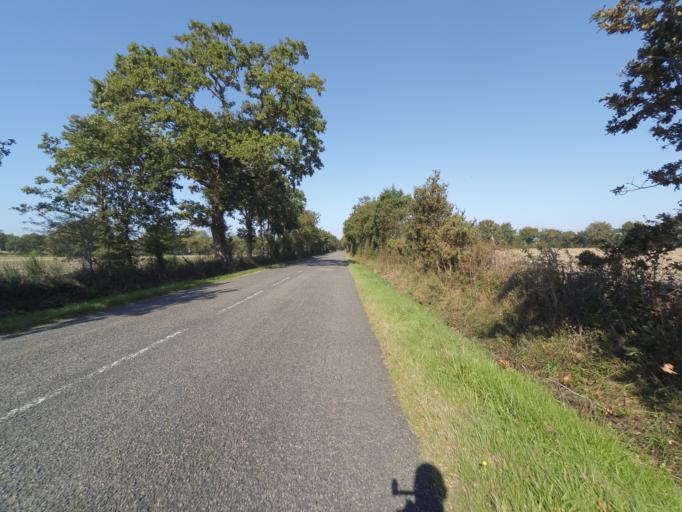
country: FR
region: Pays de la Loire
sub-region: Departement de la Loire-Atlantique
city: Chemere
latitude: 47.1123
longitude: -1.8958
